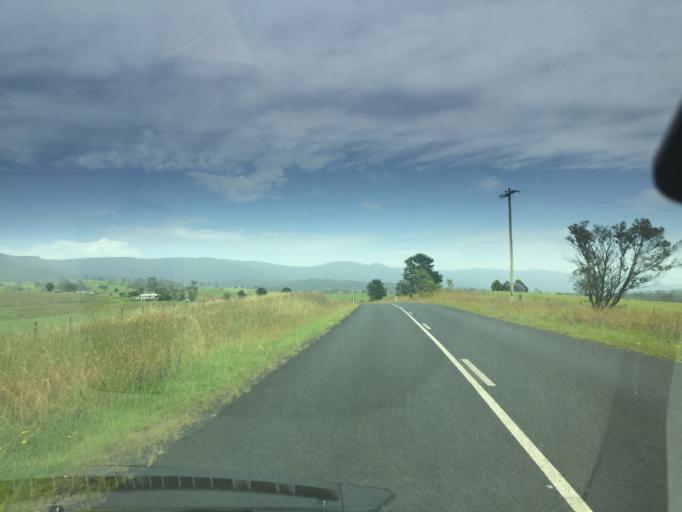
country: AU
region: New South Wales
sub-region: Bega Valley
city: Bega
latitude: -36.7291
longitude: 149.6291
